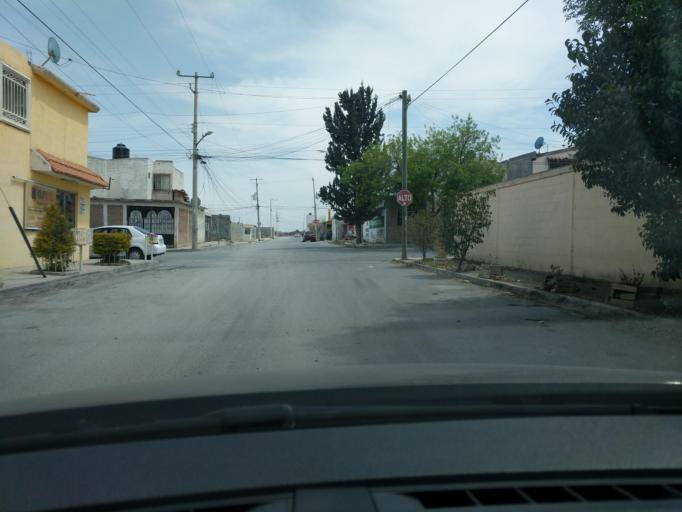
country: MX
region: Coahuila
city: Saltillo
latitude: 25.4062
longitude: -100.9379
